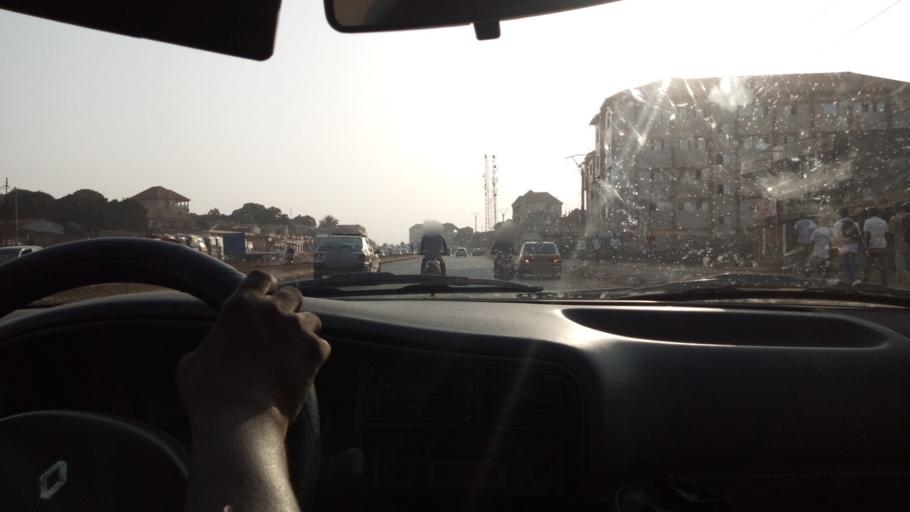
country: GN
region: Kindia
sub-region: Prefecture de Dubreka
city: Dubreka
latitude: 9.6789
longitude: -13.5401
